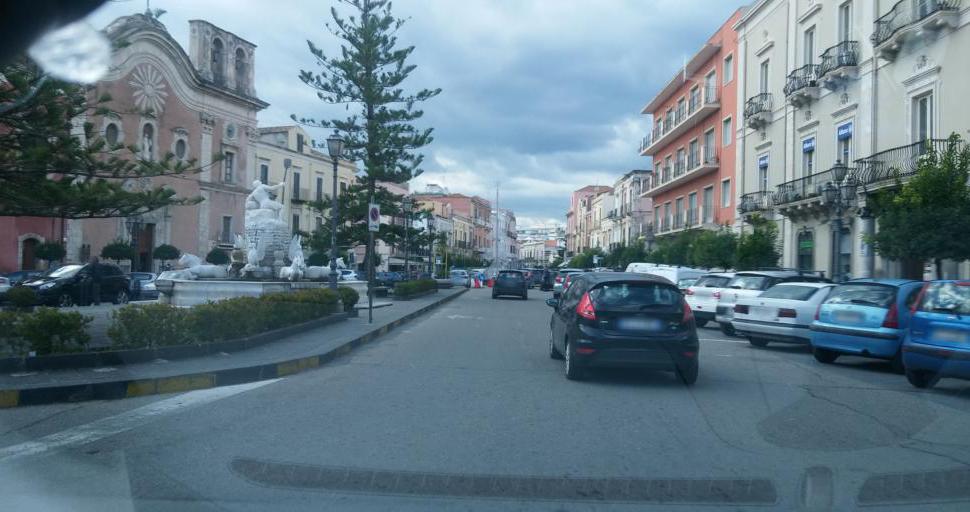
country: IT
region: Sicily
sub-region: Messina
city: Milazzo
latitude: 38.2210
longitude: 15.2416
